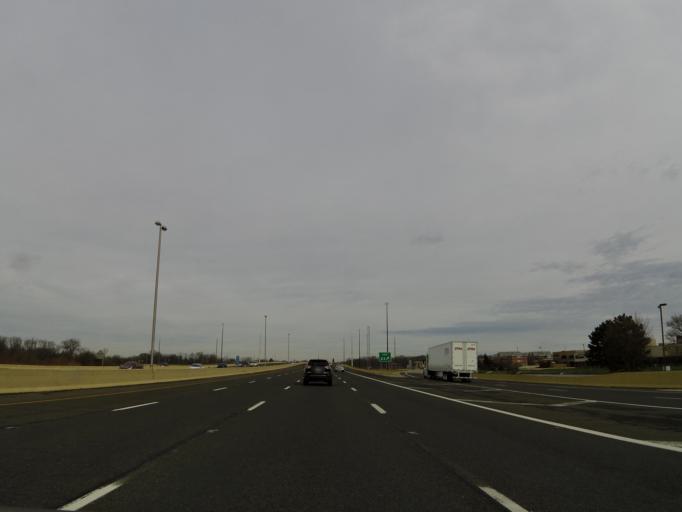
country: US
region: Indiana
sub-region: Boone County
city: Zionsville
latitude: 39.9060
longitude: -86.2698
